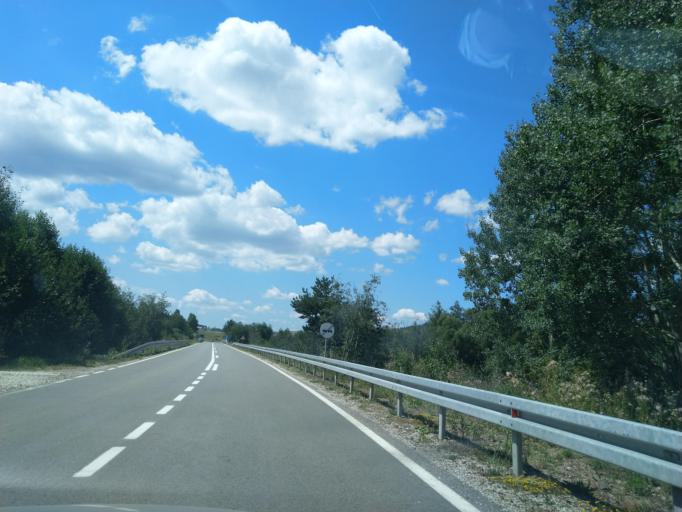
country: RS
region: Central Serbia
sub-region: Zlatiborski Okrug
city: Sjenica
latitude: 43.3283
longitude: 19.8825
